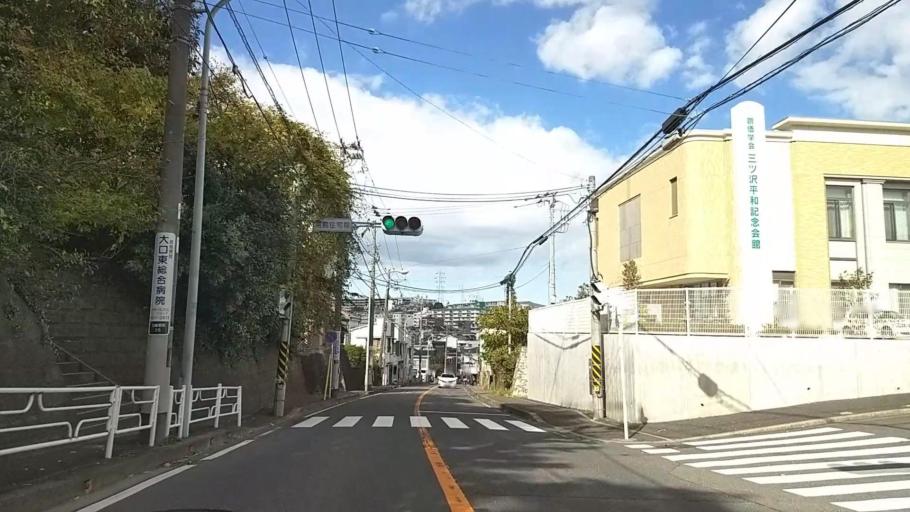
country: JP
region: Kanagawa
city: Yokohama
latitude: 35.4867
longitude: 139.6399
